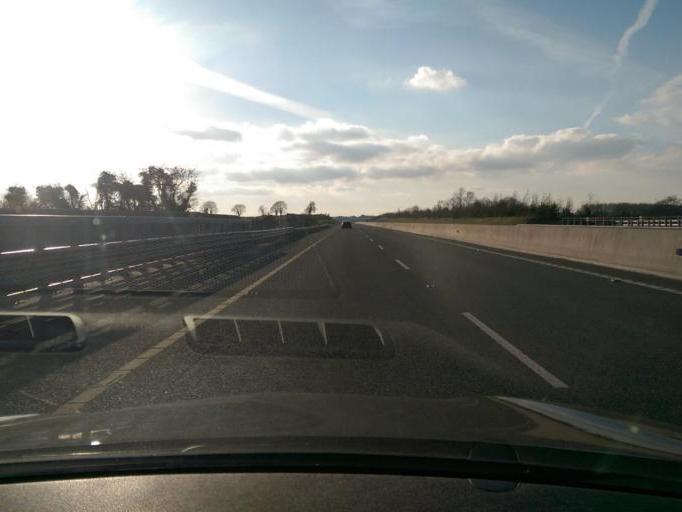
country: IE
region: Leinster
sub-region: Laois
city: Rathdowney
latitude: 52.9190
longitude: -7.5573
